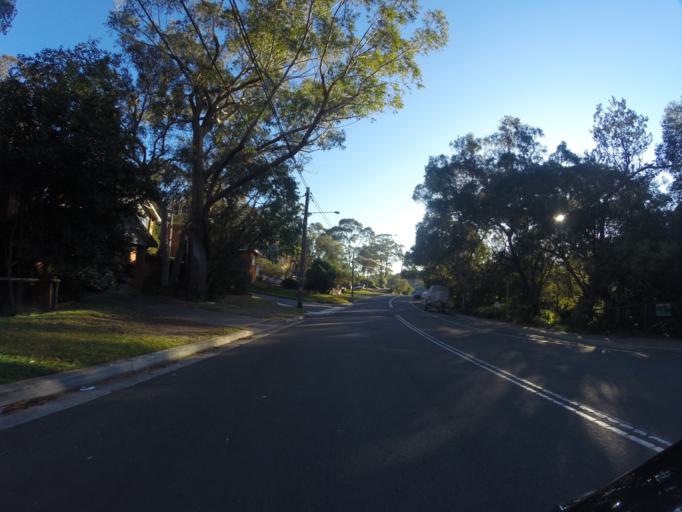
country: AU
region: New South Wales
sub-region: Sutherland Shire
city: Grays Point
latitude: -34.0572
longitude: 151.0759
